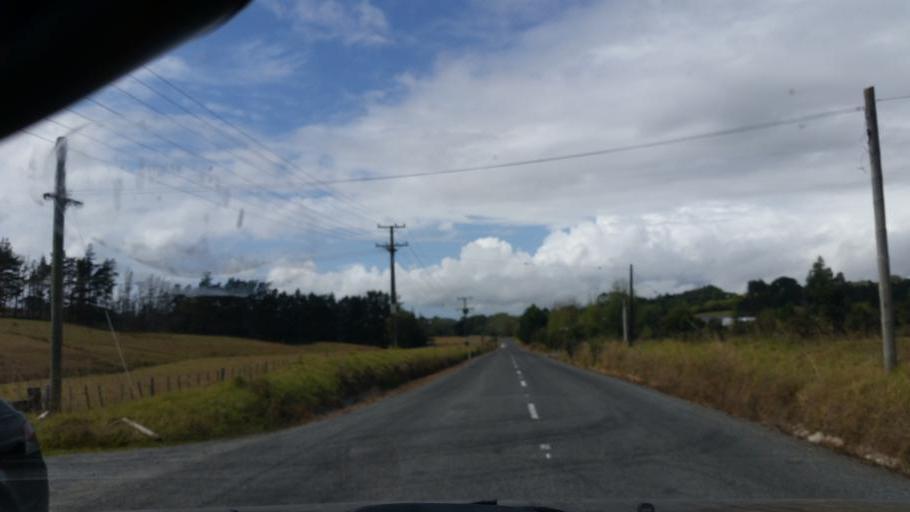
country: NZ
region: Auckland
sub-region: Auckland
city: Wellsford
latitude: -36.1189
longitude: 174.5486
